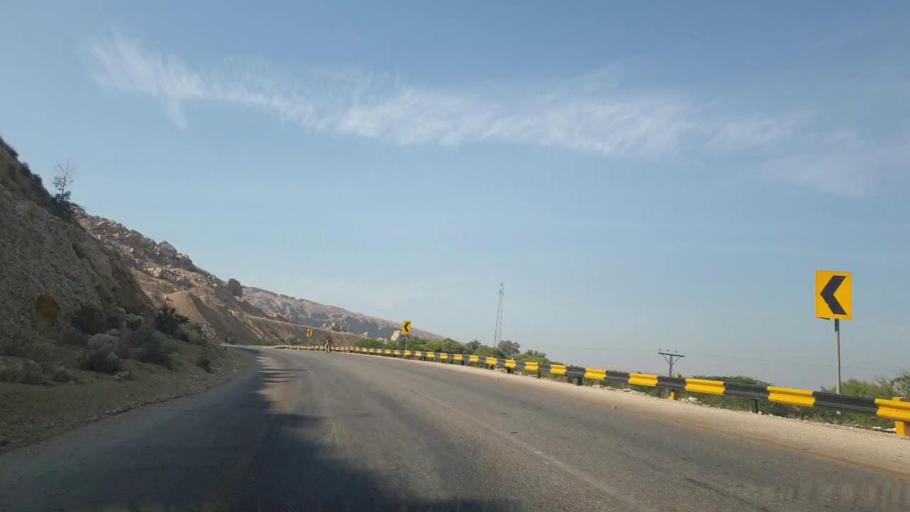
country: PK
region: Sindh
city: Sehwan
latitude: 26.3215
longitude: 67.8872
